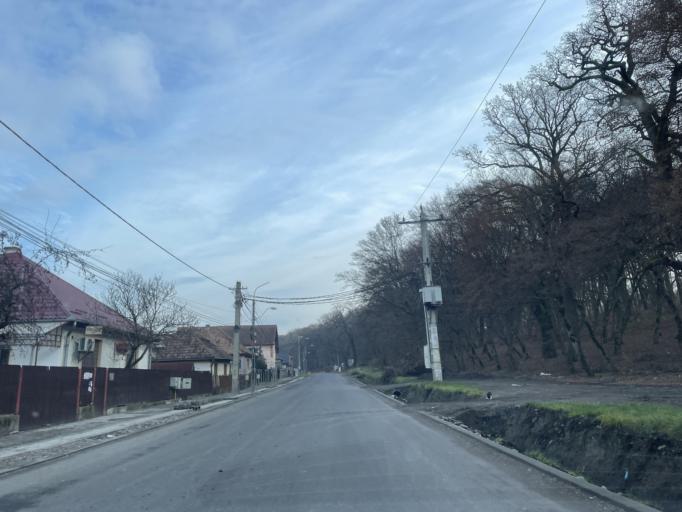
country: RO
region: Mures
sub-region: Comuna Solovastru
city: Solovastru
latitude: 46.7761
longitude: 24.7439
